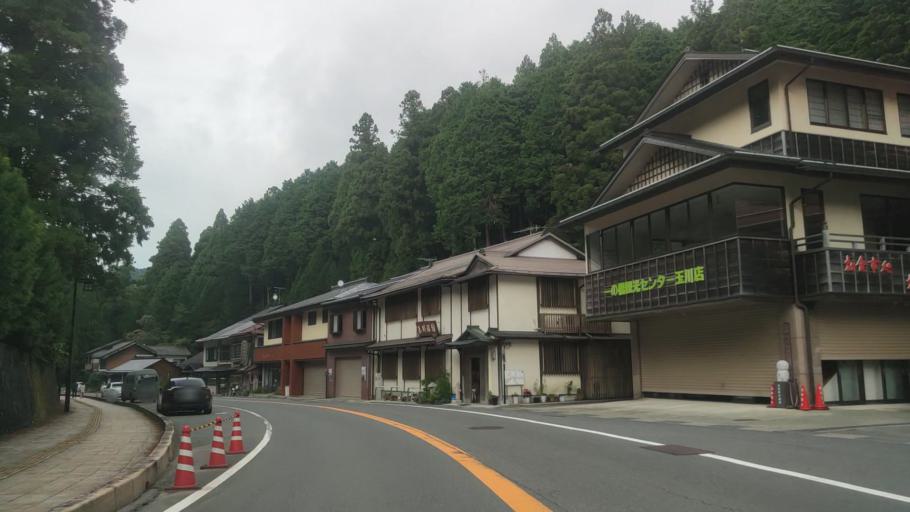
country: JP
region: Wakayama
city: Koya
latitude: 34.2145
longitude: 135.5983
